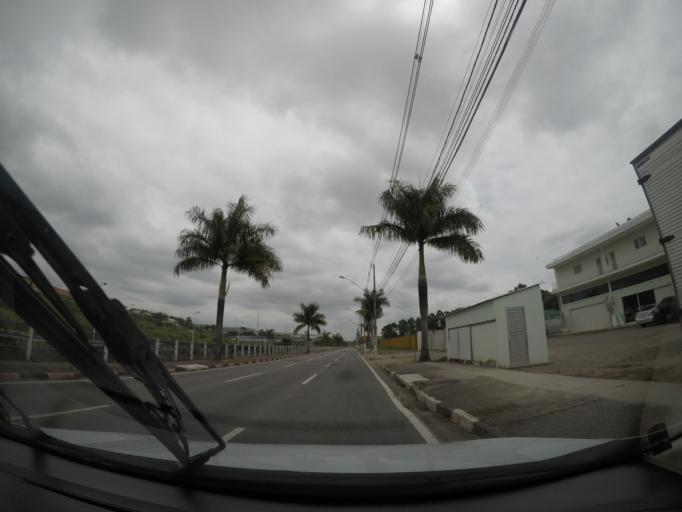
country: BR
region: Sao Paulo
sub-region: Aruja
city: Aruja
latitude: -23.4002
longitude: -46.3440
